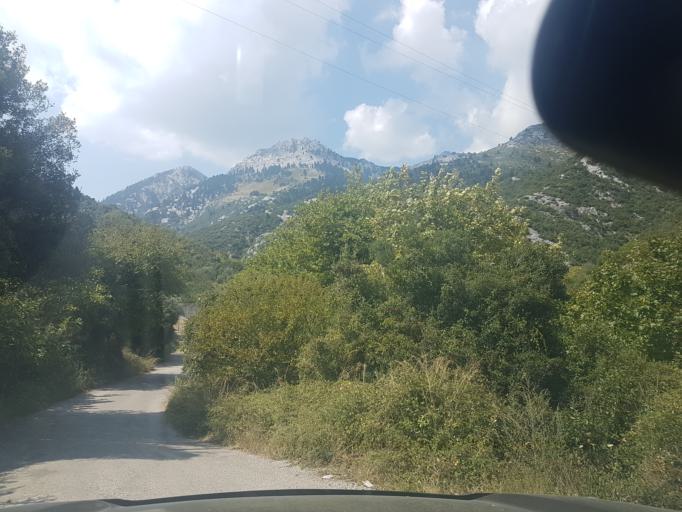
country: GR
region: Central Greece
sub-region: Nomos Evvoias
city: Yimnon
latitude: 38.6211
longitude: 23.8875
